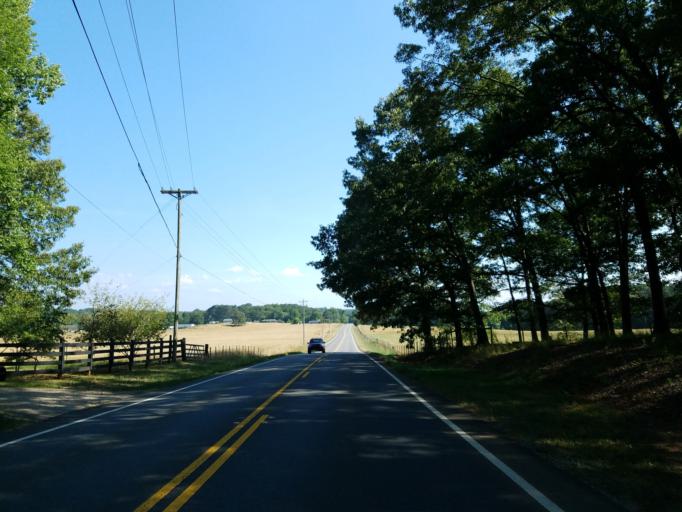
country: US
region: Georgia
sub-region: Fulton County
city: Milton
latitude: 34.2207
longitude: -84.2896
